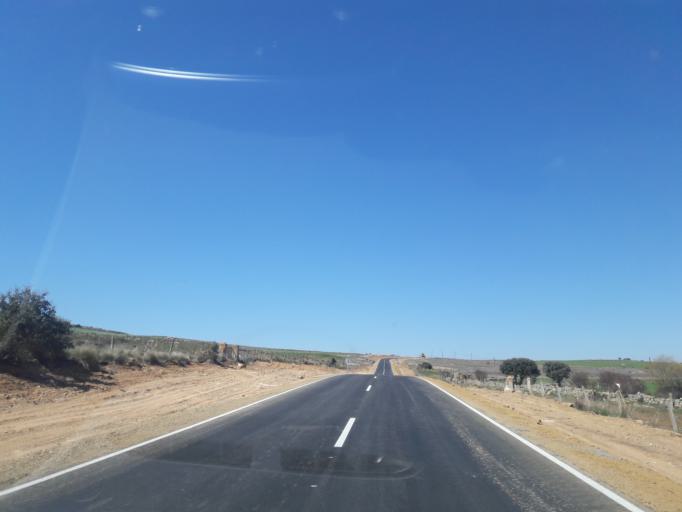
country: ES
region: Castille and Leon
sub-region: Provincia de Salamanca
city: Valdemierque
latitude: 40.8230
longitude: -5.5657
